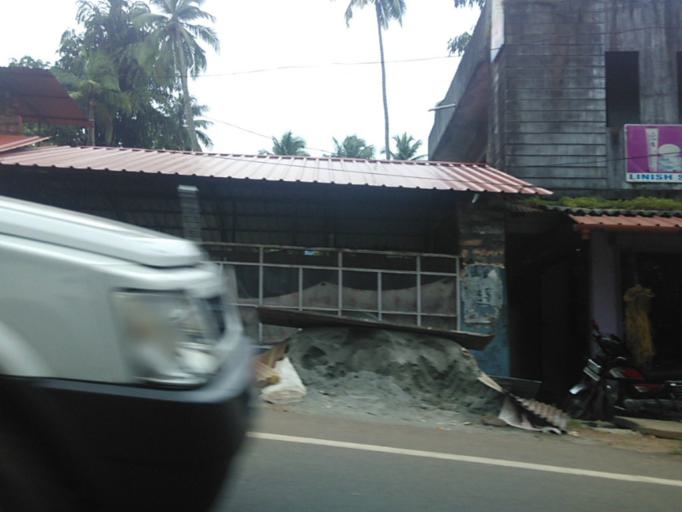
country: IN
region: Kerala
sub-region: Kozhikode
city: Kozhikode
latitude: 11.2926
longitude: 75.8182
